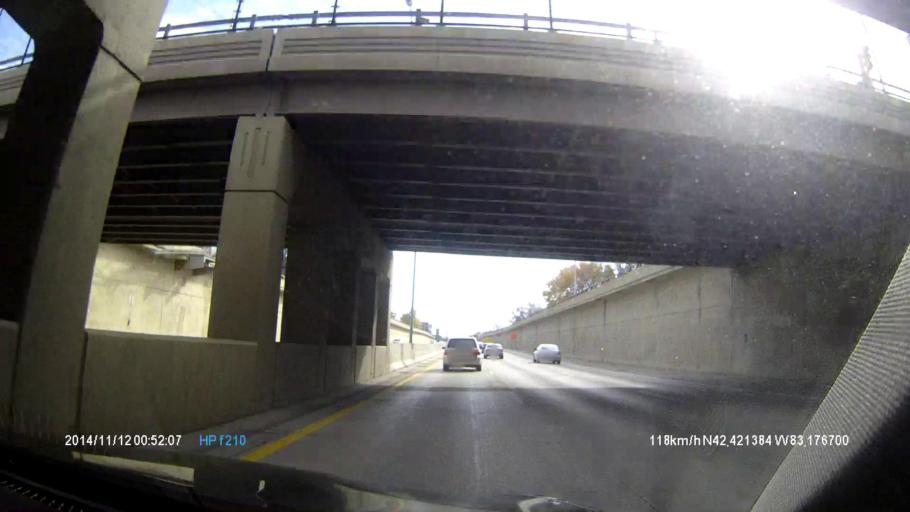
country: US
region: Michigan
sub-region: Oakland County
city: Oak Park
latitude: 42.4210
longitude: -83.1764
